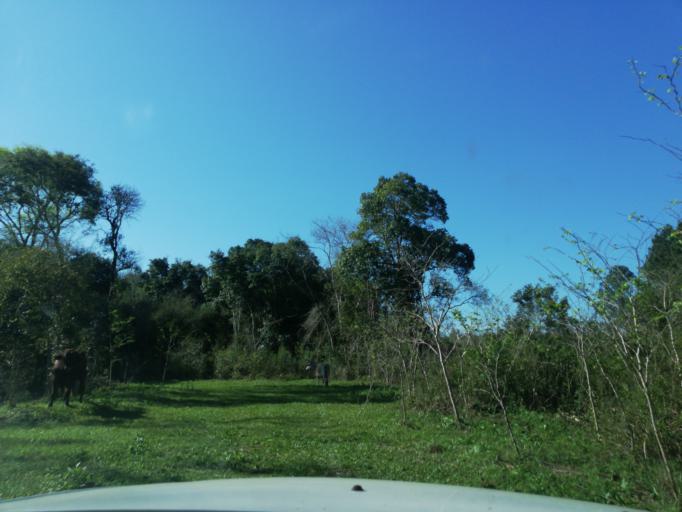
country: AR
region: Misiones
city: Arroyo del Medio
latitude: -27.6777
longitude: -55.3974
